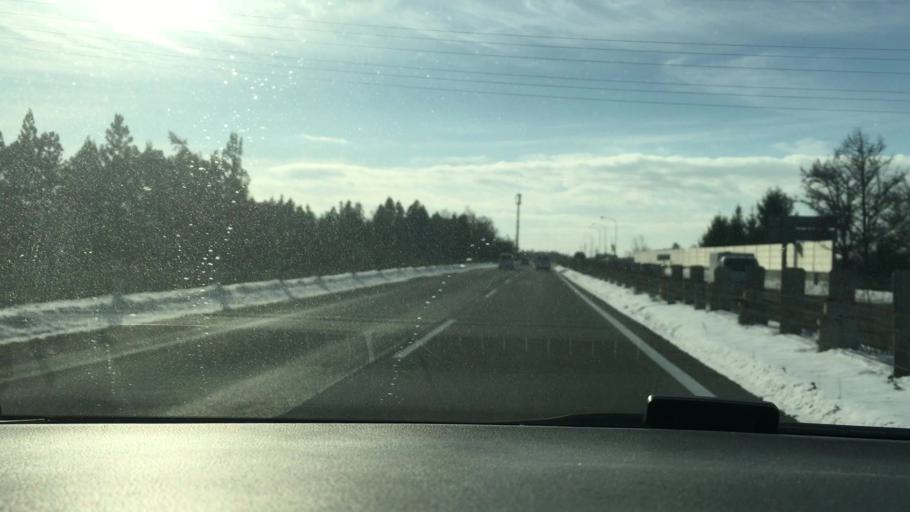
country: JP
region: Iwate
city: Hanamaki
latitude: 39.3462
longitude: 141.0905
